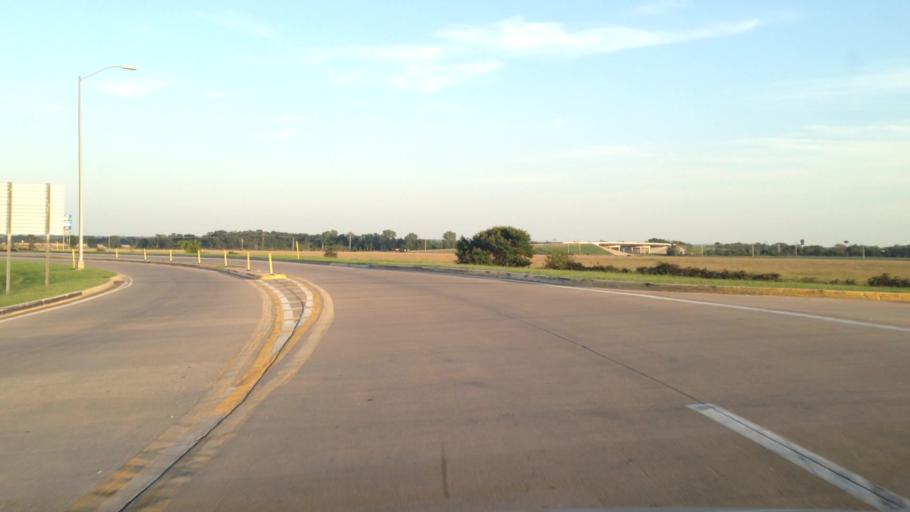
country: US
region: Oklahoma
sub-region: Ottawa County
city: Afton
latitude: 36.7190
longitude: -94.9336
